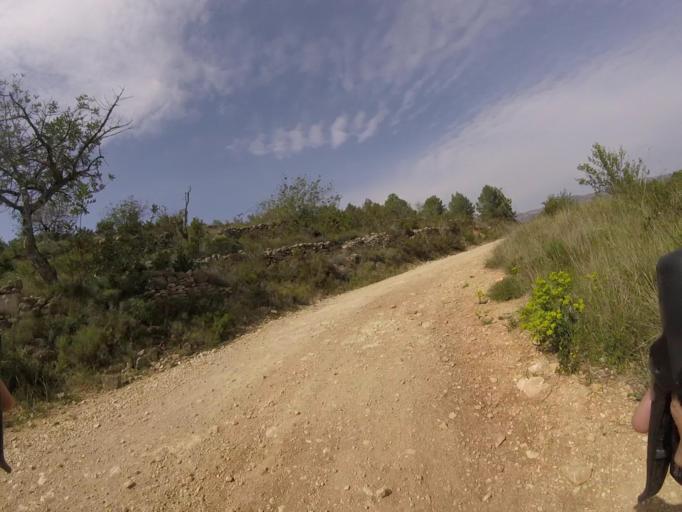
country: ES
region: Valencia
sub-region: Provincia de Castello
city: Cuevas de Vinroma
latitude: 40.2909
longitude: 0.1276
